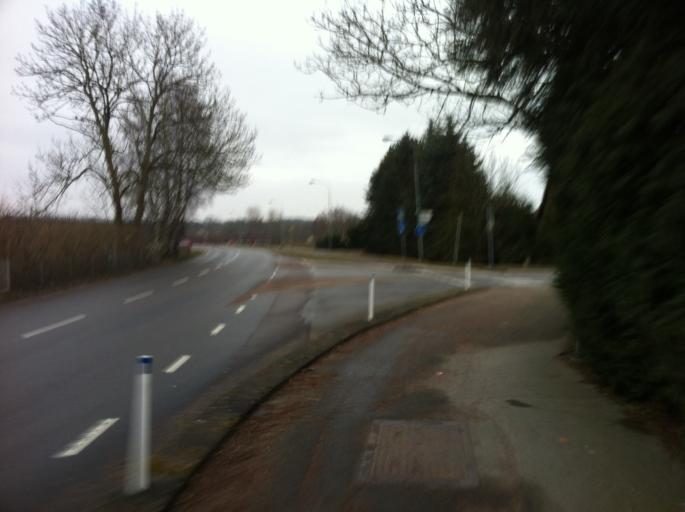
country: SE
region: Skane
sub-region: Hoors Kommun
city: Satofta
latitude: 55.9098
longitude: 13.5535
